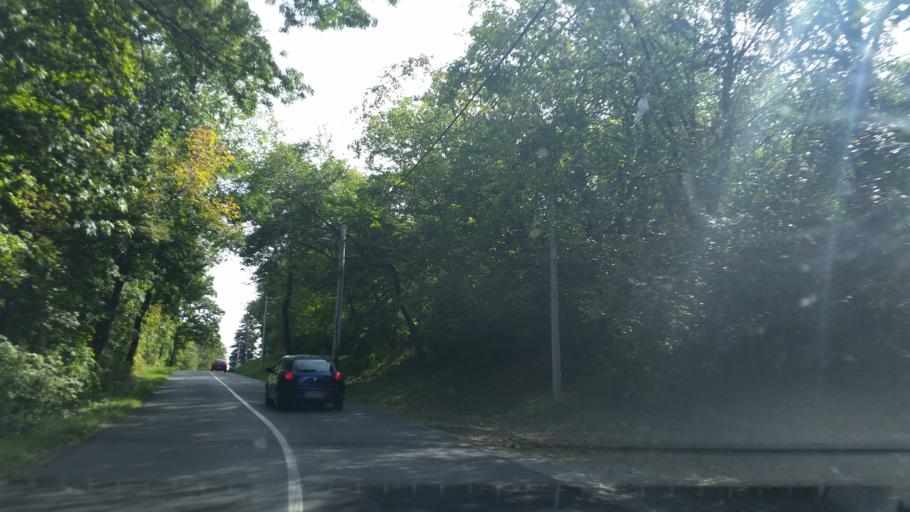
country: RS
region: Central Serbia
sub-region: Belgrade
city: Palilula
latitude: 44.8071
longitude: 20.5075
